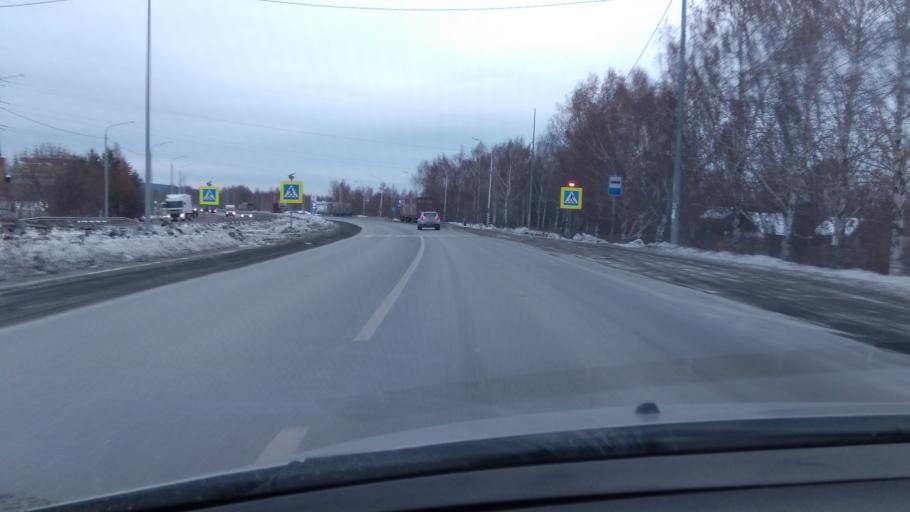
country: RU
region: Sverdlovsk
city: Aramil
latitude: 56.7032
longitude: 60.7482
